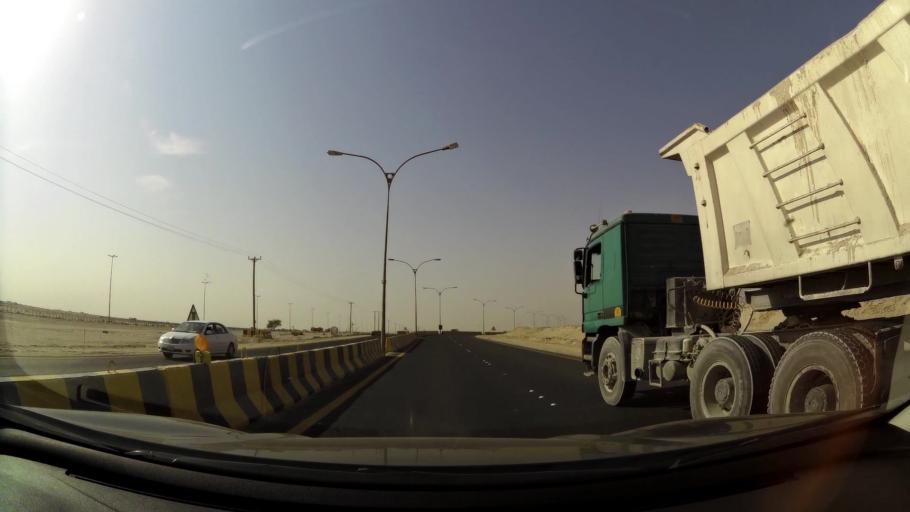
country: KW
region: Al Ahmadi
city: Al Ahmadi
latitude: 28.8970
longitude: 48.0881
